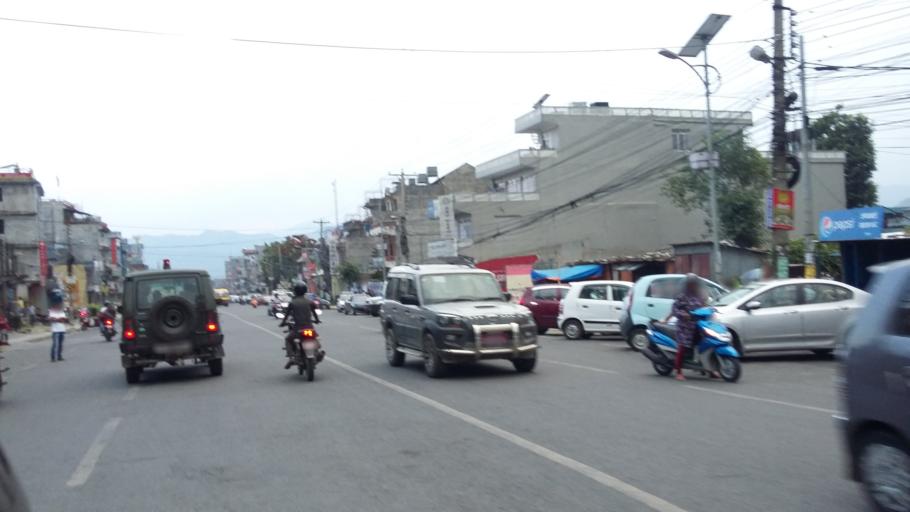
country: NP
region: Western Region
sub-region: Gandaki Zone
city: Pokhara
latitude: 28.2195
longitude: 83.9869
